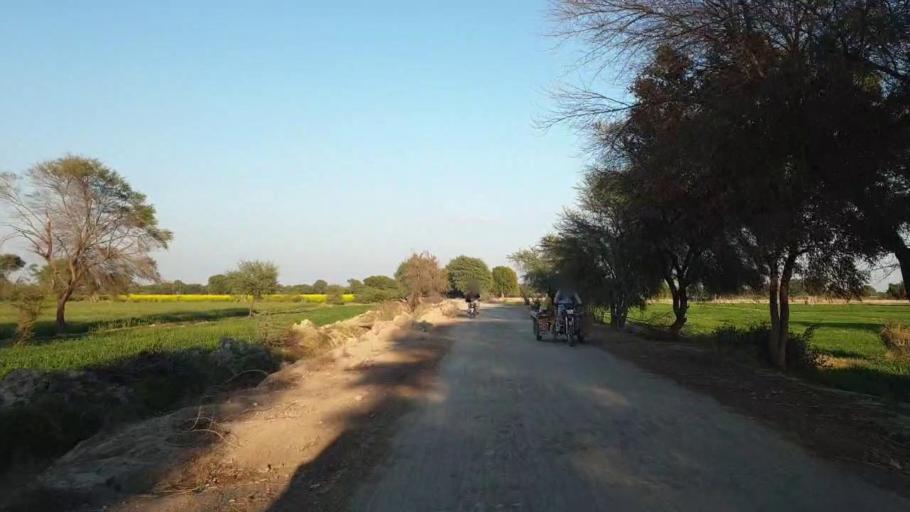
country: PK
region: Sindh
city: Shahpur Chakar
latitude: 26.1408
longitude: 68.5668
